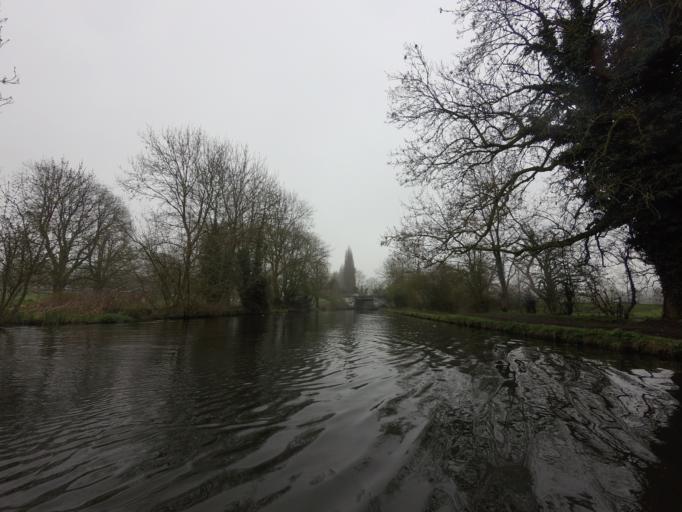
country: GB
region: England
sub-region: Hertfordshire
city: Hemel Hempstead
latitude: 51.7443
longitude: -0.4832
